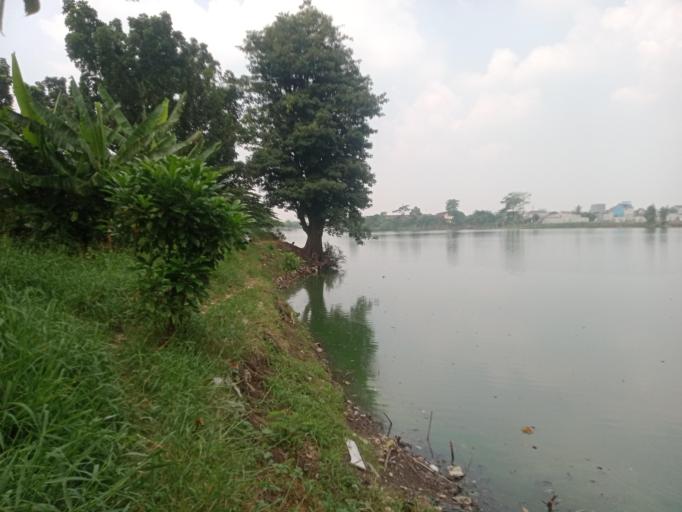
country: ID
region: West Java
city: Sepatan
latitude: -6.1602
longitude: 106.5818
